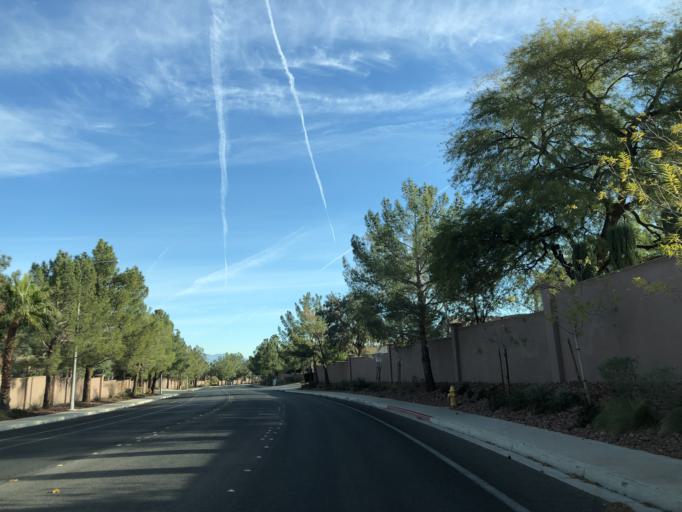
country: US
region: Nevada
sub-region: Clark County
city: Whitney
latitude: 36.0220
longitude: -115.0720
